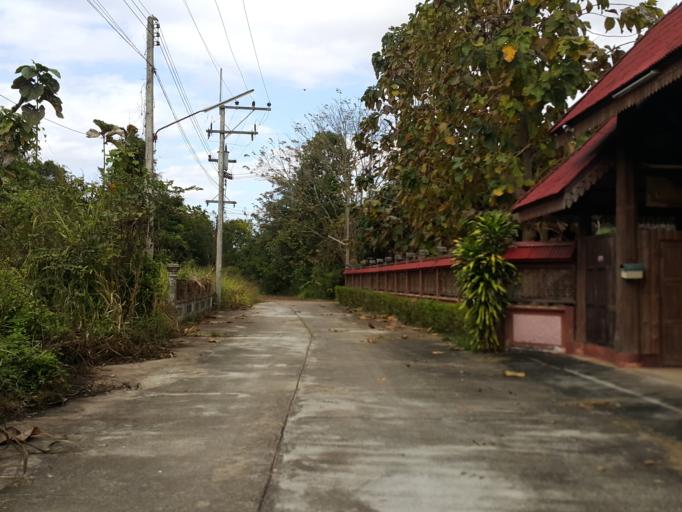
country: TH
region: Chiang Mai
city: San Sai
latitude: 18.8644
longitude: 99.0994
